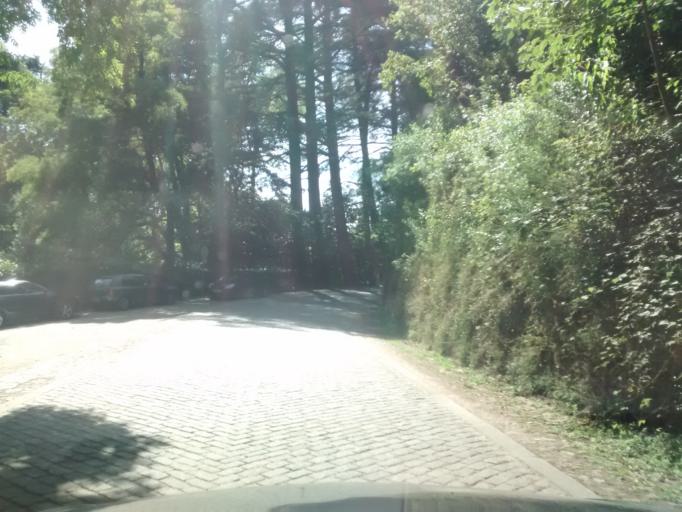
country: PT
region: Aveiro
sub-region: Mealhada
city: Pampilhosa do Botao
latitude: 40.3785
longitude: -8.3673
